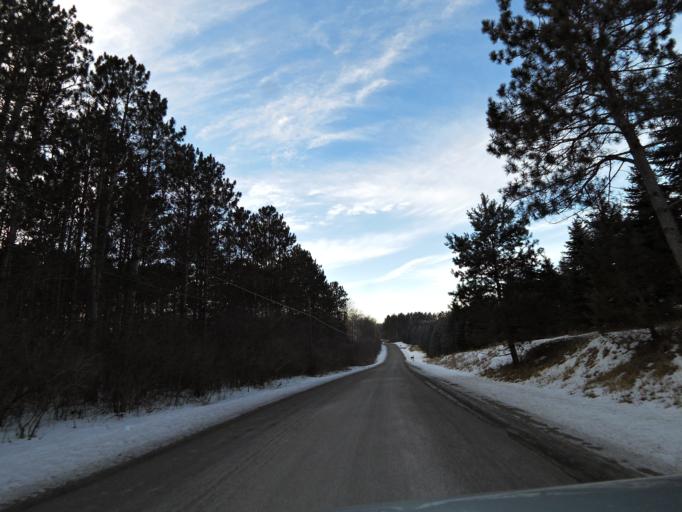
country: US
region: Minnesota
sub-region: Washington County
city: Afton
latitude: 44.9296
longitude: -92.8046
